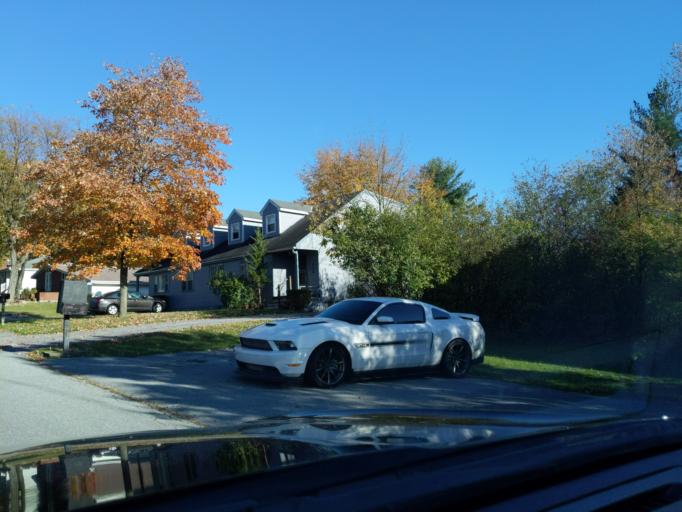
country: US
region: Pennsylvania
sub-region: Blair County
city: Lakemont
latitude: 40.4550
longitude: -78.3933
